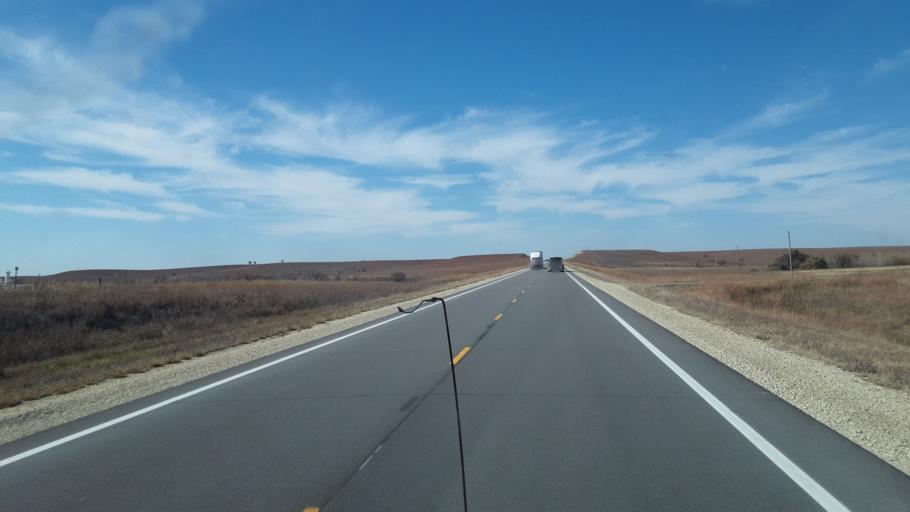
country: US
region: Kansas
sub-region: Chase County
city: Cottonwood Falls
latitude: 38.3627
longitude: -96.7559
